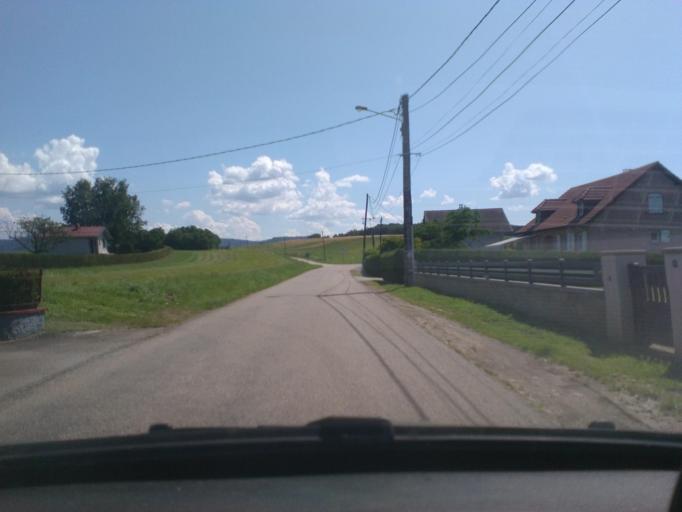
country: FR
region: Lorraine
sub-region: Departement des Vosges
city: Etival-Clairefontaine
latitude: 48.3531
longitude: 6.8652
